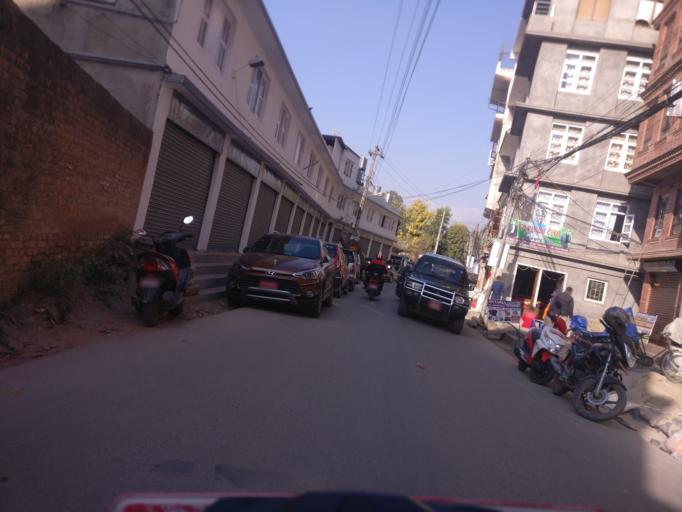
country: NP
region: Central Region
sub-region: Bagmati Zone
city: Patan
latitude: 27.6772
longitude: 85.3203
